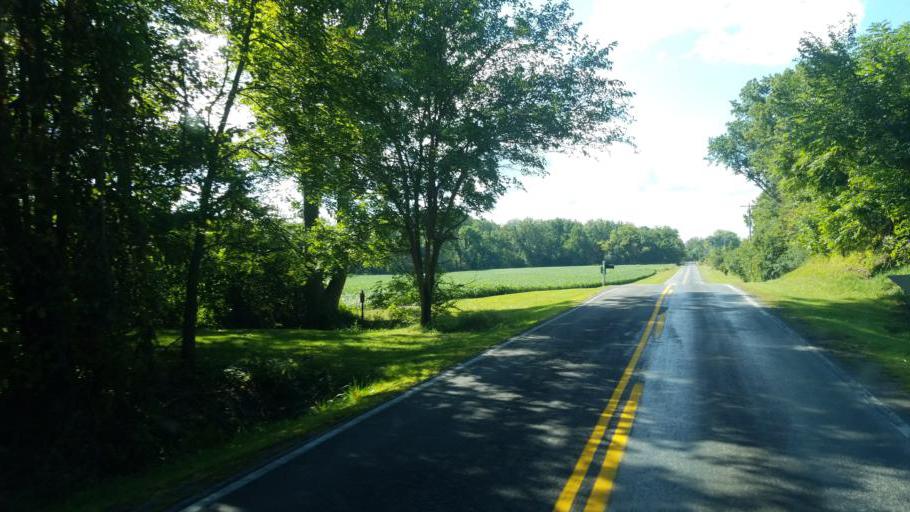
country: US
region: Ohio
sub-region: Lorain County
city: Oberlin
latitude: 41.2732
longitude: -82.1791
